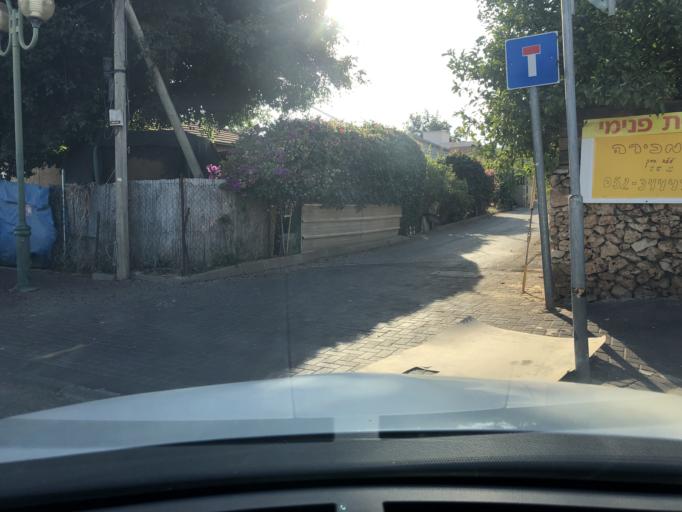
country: IL
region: Central District
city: Hod HaSharon
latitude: 32.1398
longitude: 34.9032
